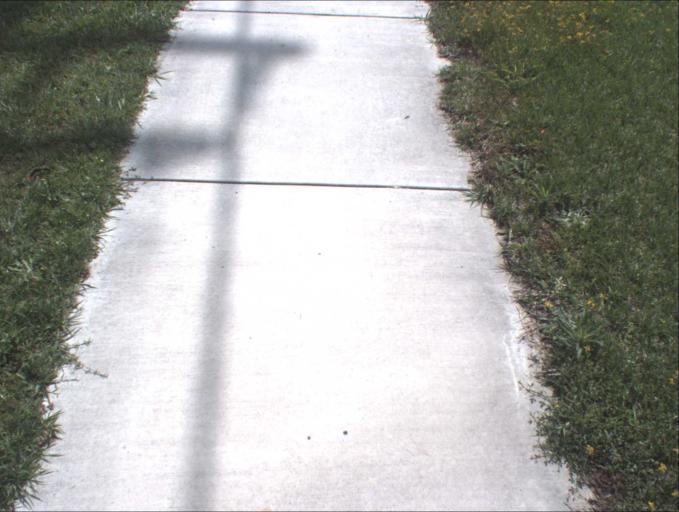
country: AU
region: Queensland
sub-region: Logan
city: Park Ridge South
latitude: -27.7283
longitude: 153.0353
